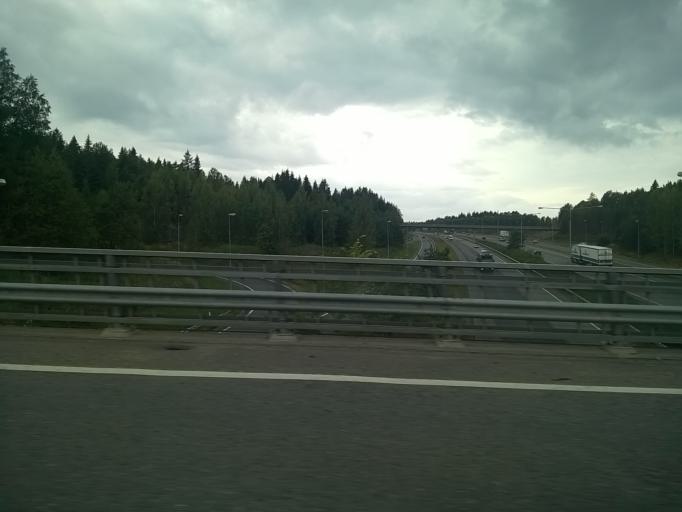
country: FI
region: Pirkanmaa
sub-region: Tampere
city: Tampere
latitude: 61.4690
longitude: 23.8399
